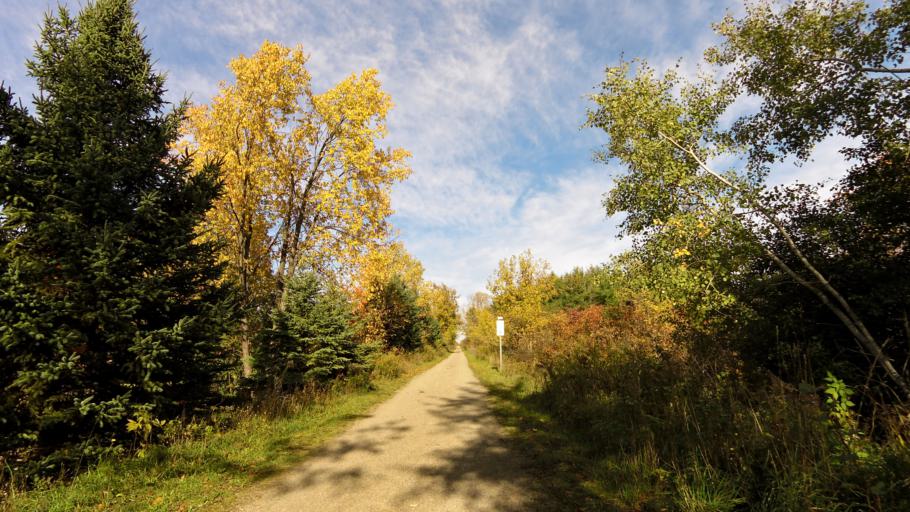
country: CA
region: Ontario
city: Orangeville
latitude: 43.7889
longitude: -80.0527
